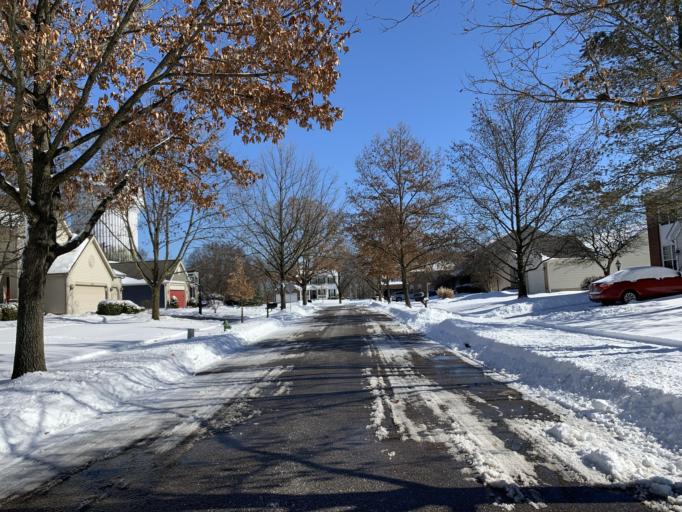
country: US
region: Ohio
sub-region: Franklin County
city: Dublin
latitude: 40.1265
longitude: -83.1650
